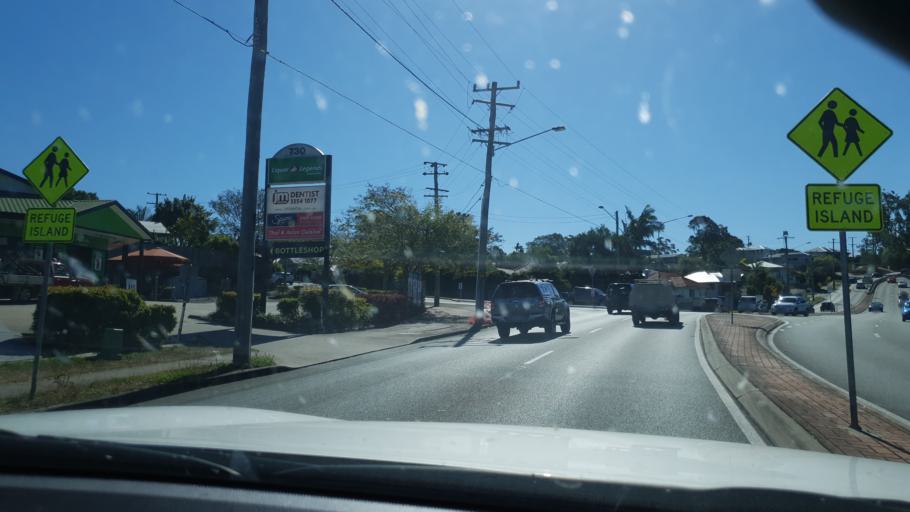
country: AU
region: Queensland
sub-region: Brisbane
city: Everton Park
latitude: -27.4011
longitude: 152.9868
